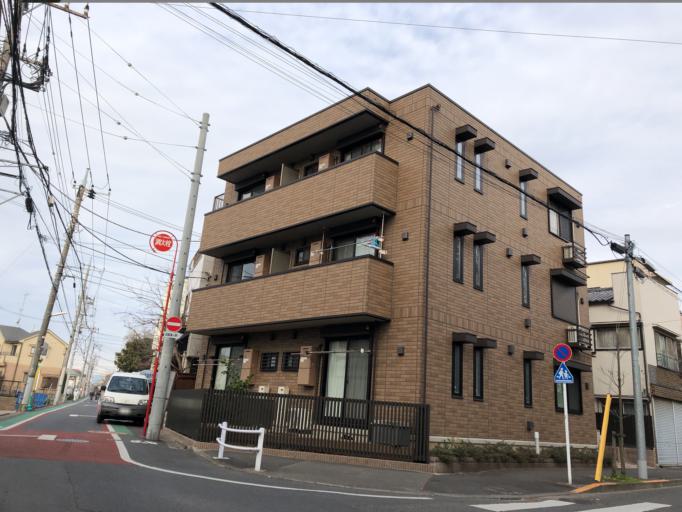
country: JP
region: Tokyo
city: Kamirenjaku
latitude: 35.6963
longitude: 139.5442
